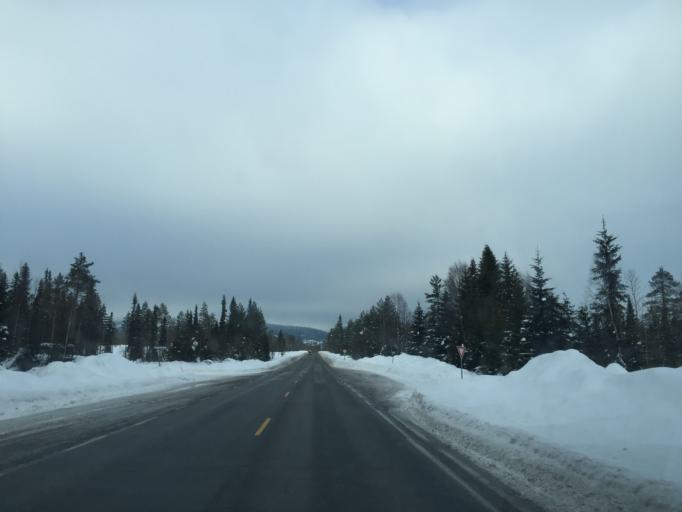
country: NO
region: Hedmark
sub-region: Trysil
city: Innbygda
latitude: 61.1483
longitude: 12.1286
